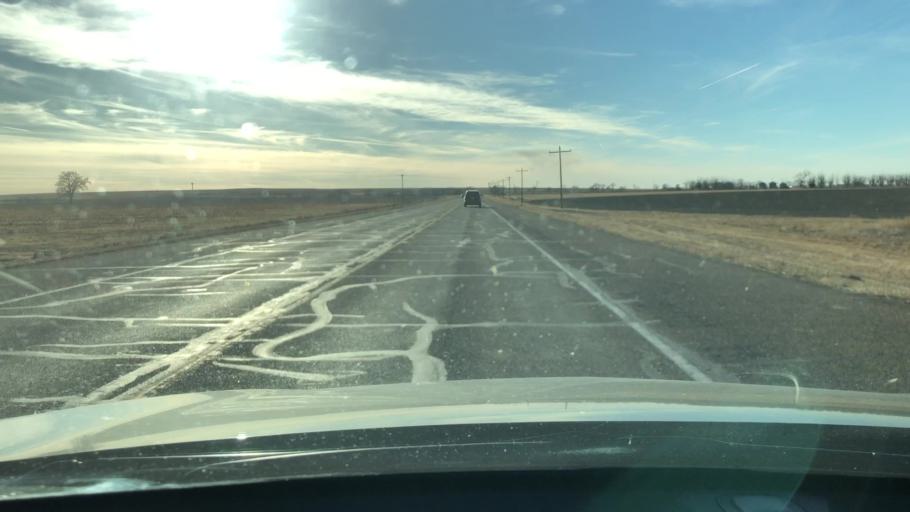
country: US
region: Colorado
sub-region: Prowers County
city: Lamar
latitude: 38.0640
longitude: -102.3395
